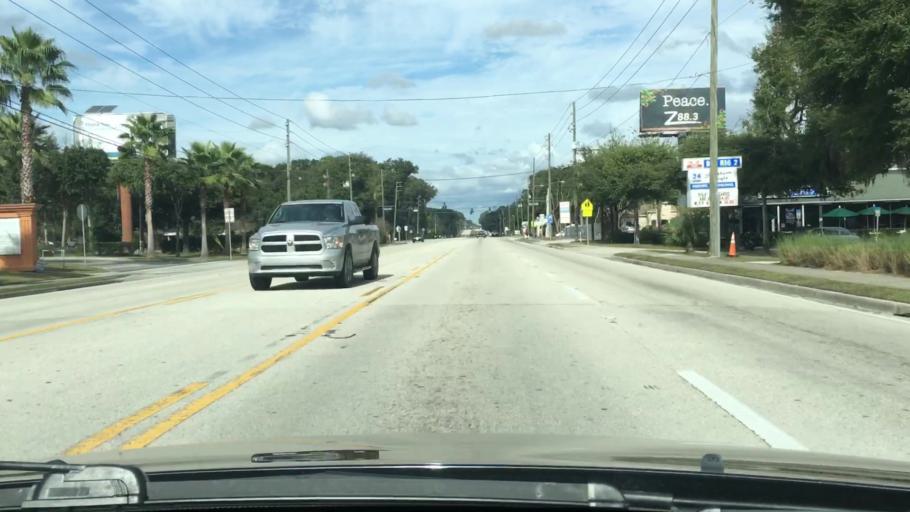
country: US
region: Florida
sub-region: Volusia County
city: DeLand
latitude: 29.0409
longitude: -81.3246
